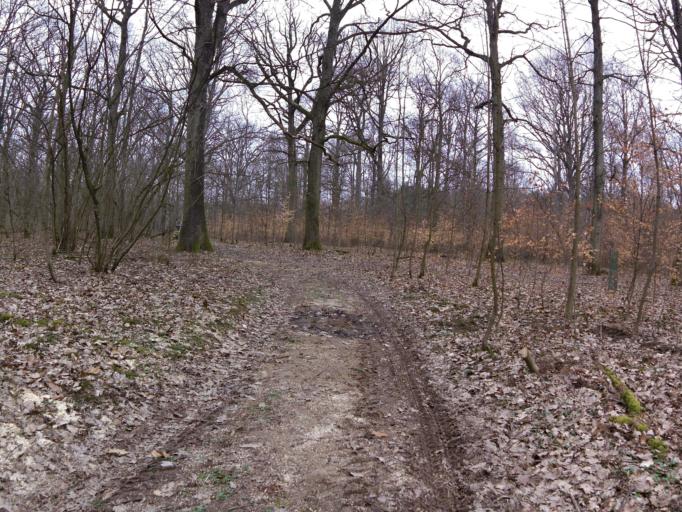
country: DE
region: Bavaria
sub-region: Regierungsbezirk Unterfranken
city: Rottendorf
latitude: 49.8110
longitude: 10.0383
